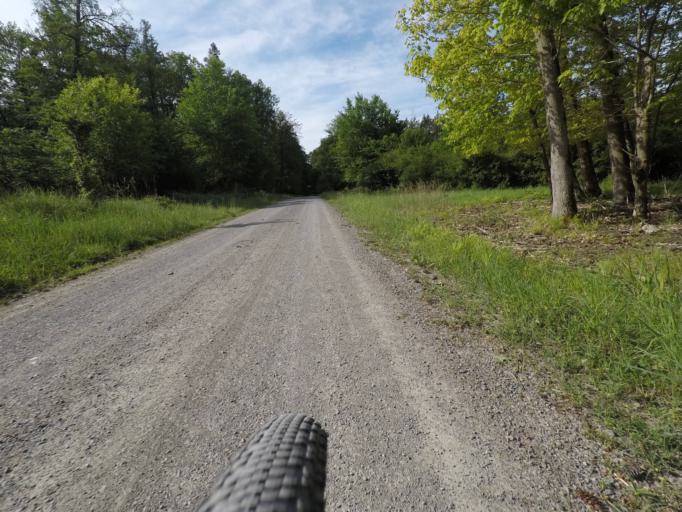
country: DE
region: Baden-Wuerttemberg
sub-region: Regierungsbezirk Stuttgart
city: Weil im Schonbuch
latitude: 48.5735
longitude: 9.0600
